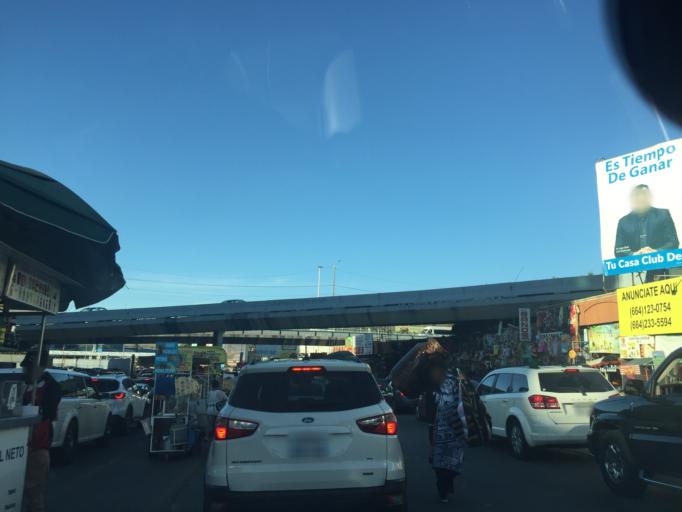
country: MX
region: Baja California
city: Tijuana
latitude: 32.5394
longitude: -117.0273
